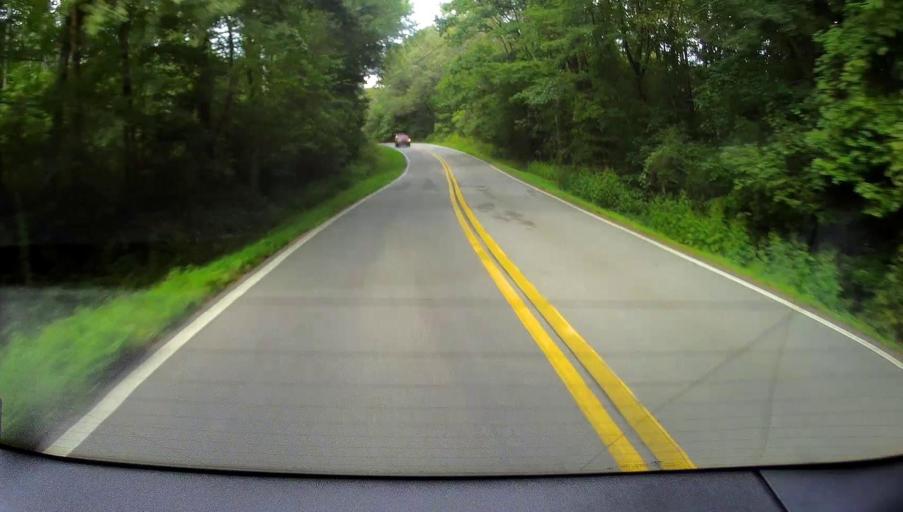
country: US
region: Georgia
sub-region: Catoosa County
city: Ringgold
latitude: 34.9154
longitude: -85.0864
